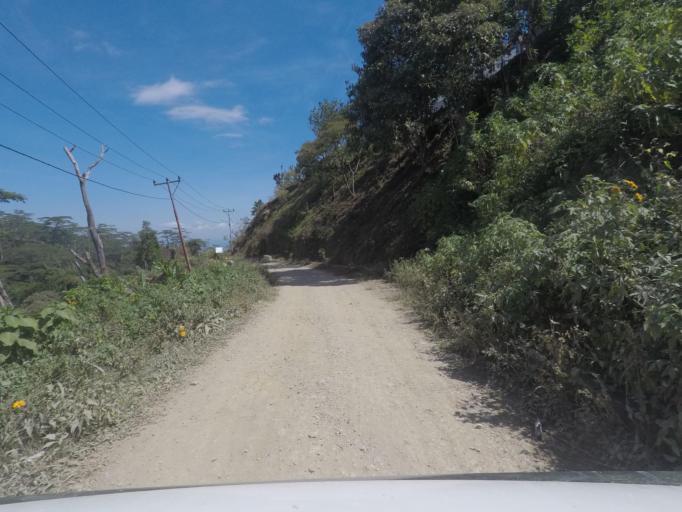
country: TL
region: Ermera
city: Gleno
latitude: -8.7530
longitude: 125.3267
